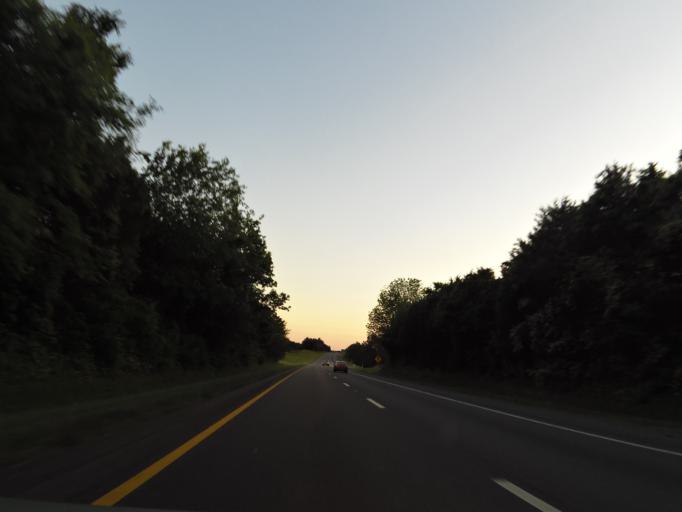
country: US
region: Tennessee
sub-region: Jefferson County
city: White Pine
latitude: 36.0916
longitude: -83.3539
